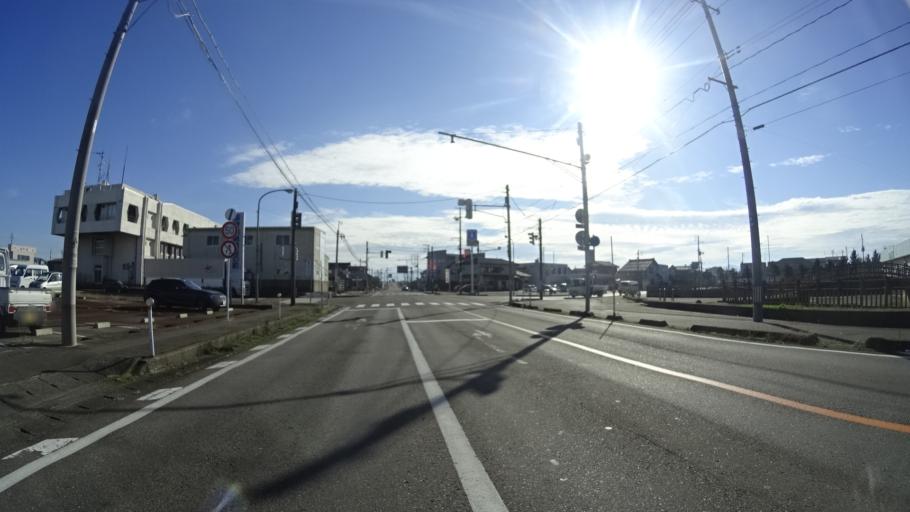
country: JP
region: Niigata
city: Mitsuke
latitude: 37.5478
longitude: 138.8765
